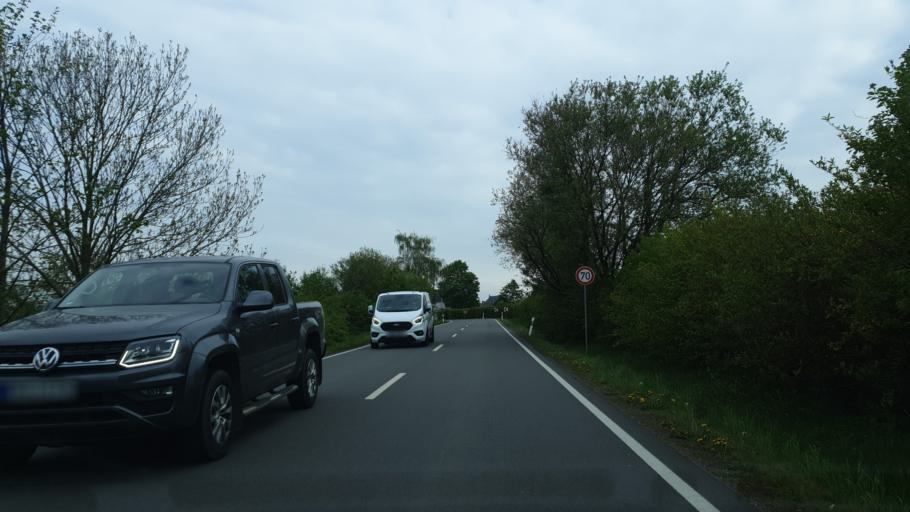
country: DE
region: Saxony
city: Gersdorf
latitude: 50.7529
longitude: 12.7213
